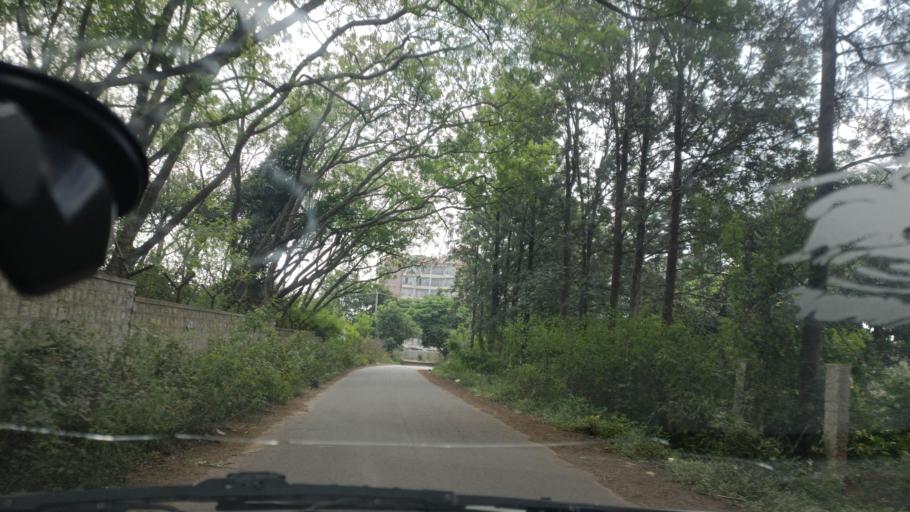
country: IN
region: Karnataka
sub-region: Bangalore Urban
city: Yelahanka
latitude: 13.1563
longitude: 77.6411
